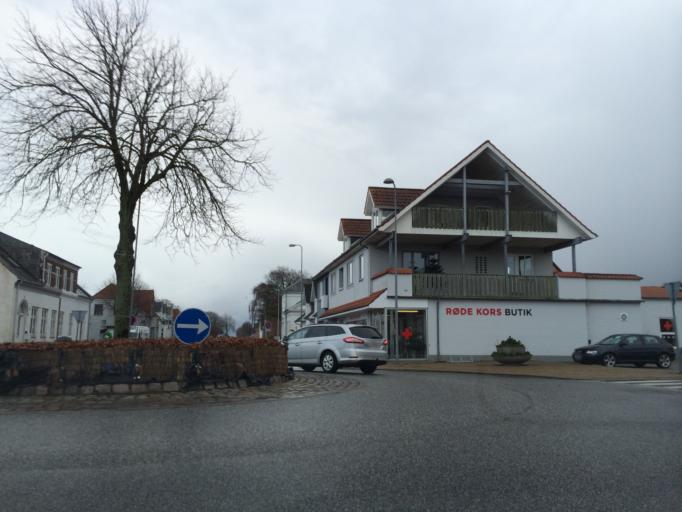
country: DK
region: Central Jutland
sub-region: Ringkobing-Skjern Kommune
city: Skjern
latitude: 55.9456
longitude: 8.4952
